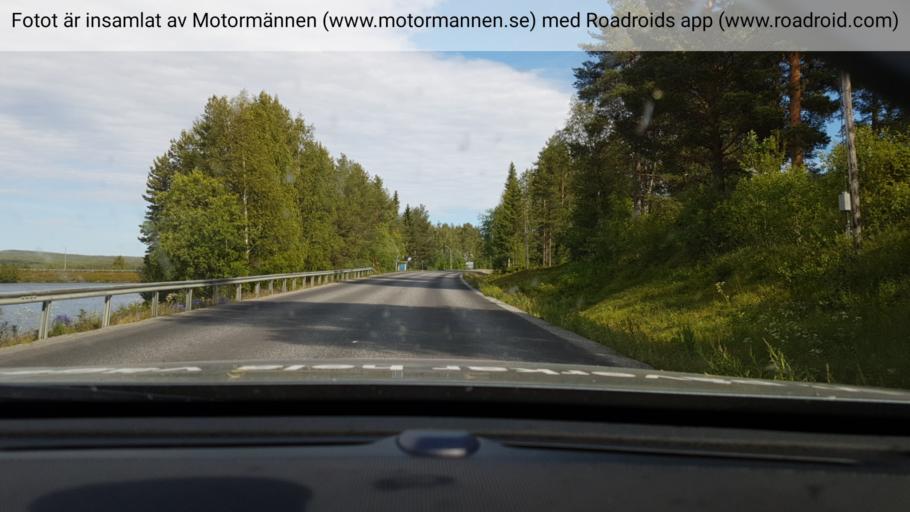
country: SE
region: Vaesterbotten
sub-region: Lycksele Kommun
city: Soderfors
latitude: 64.8282
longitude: 18.0454
